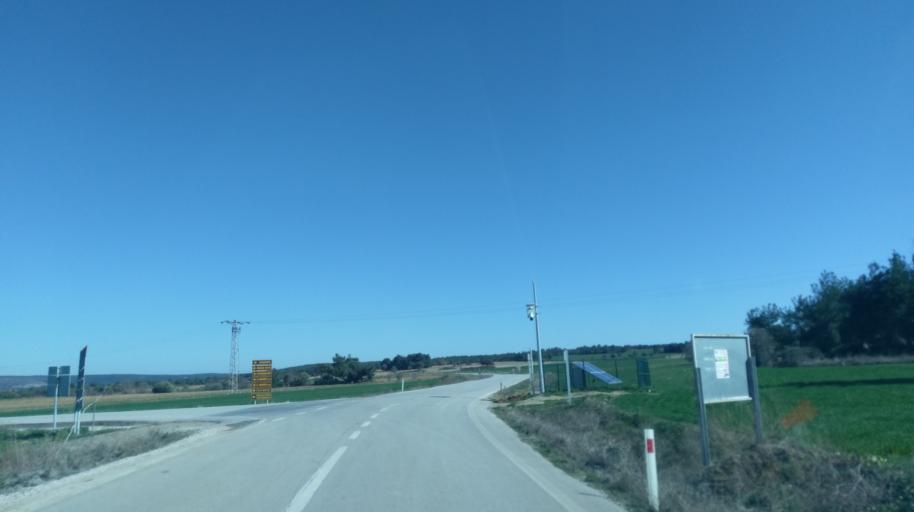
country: TR
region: Canakkale
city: Intepe
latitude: 40.1065
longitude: 26.2358
